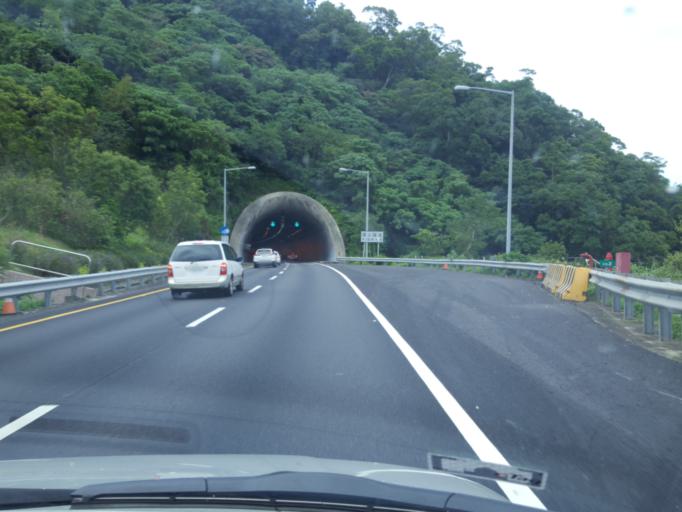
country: TW
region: Taiwan
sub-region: Yilan
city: Yilan
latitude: 24.8471
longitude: 121.7913
